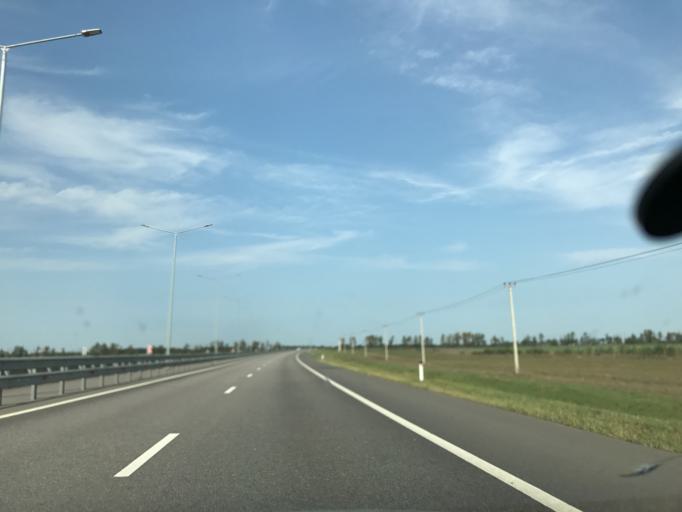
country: RU
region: Voronezj
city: Podkletnoye
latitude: 51.5171
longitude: 39.5114
